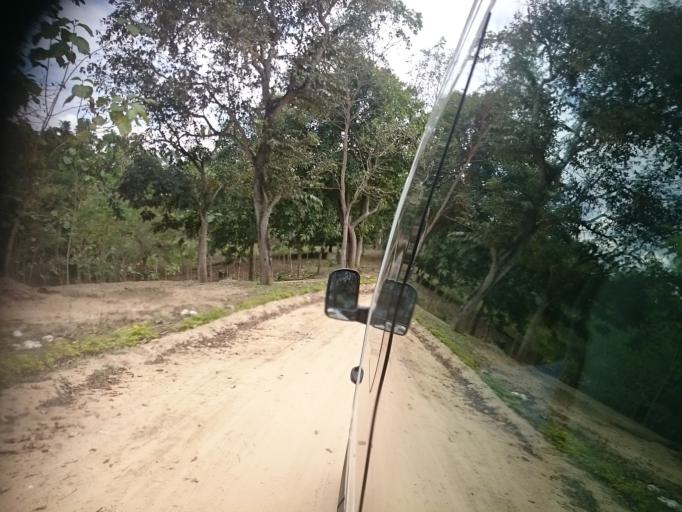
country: PE
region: San Martin
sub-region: Provincia de San Martin
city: Tarapoto
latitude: -6.5114
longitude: -76.3415
